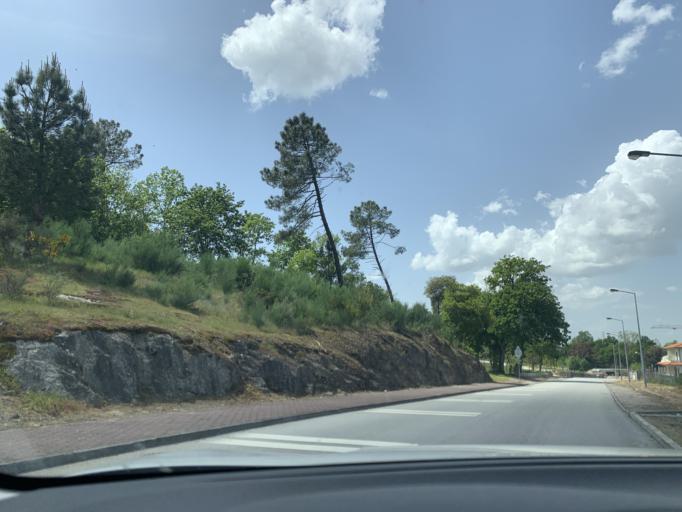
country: PT
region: Viseu
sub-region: Mangualde
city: Mangualde
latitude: 40.6083
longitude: -7.7675
